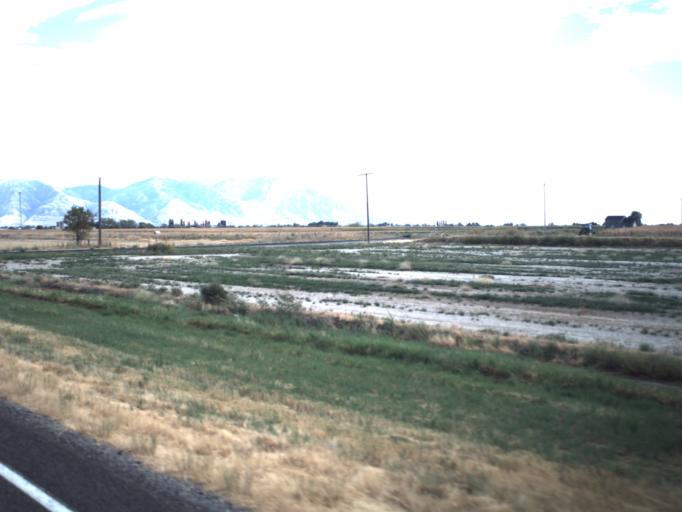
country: US
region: Utah
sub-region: Box Elder County
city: Elwood
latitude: 41.5696
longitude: -112.1995
